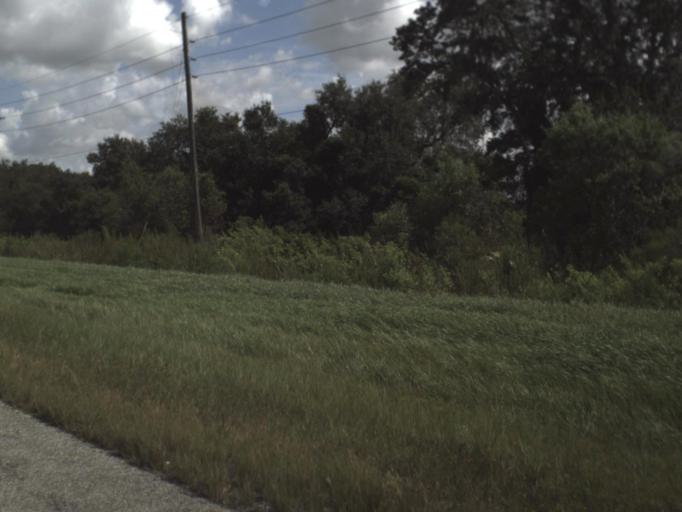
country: US
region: Florida
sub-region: Charlotte County
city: Cleveland
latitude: 26.9972
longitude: -81.9589
